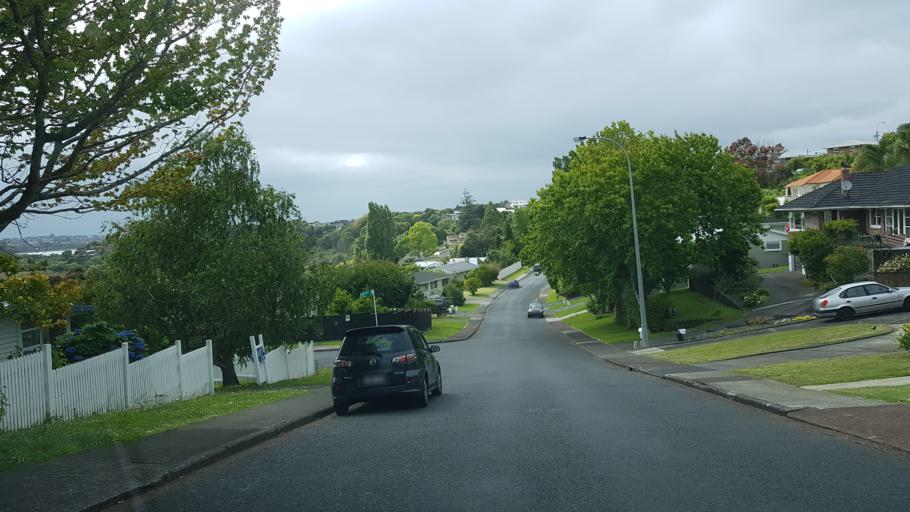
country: NZ
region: Auckland
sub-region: Auckland
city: North Shore
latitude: -36.8027
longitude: 174.7485
